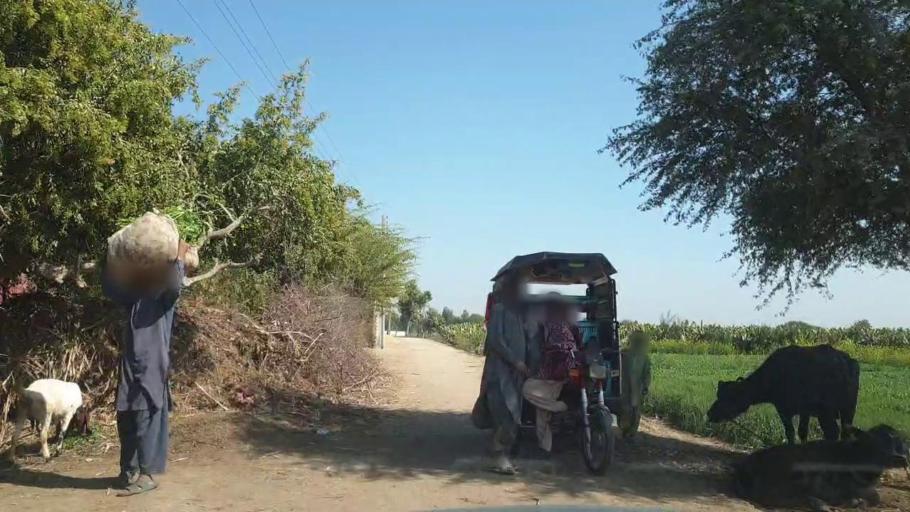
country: PK
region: Sindh
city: Tando Adam
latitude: 25.6496
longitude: 68.6975
